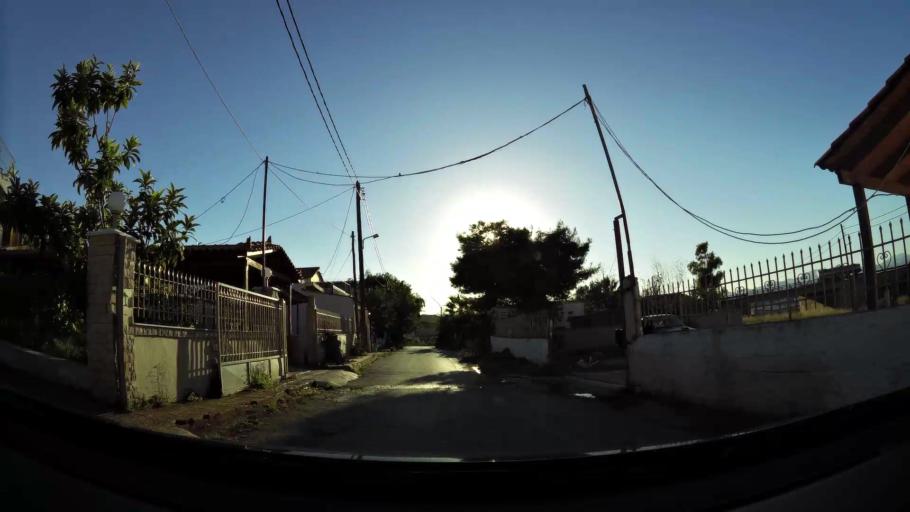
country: GR
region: Attica
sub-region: Nomarchia Athinas
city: Skaramangas
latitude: 38.0329
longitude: 23.6181
